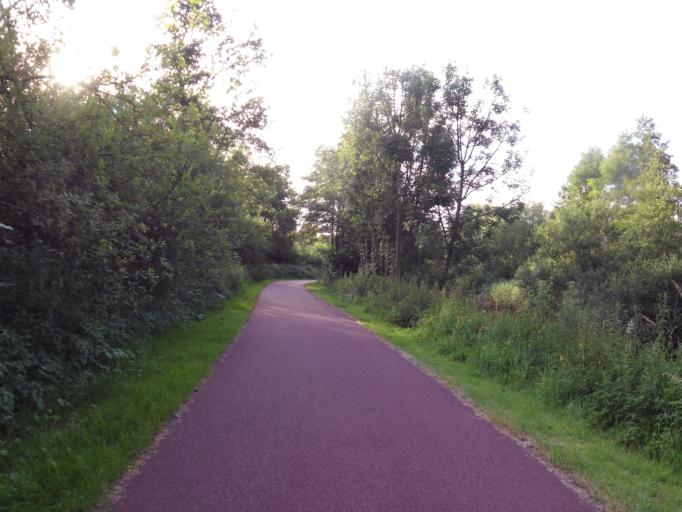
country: NL
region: North Brabant
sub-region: Gemeente Geldrop-Mierlo
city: Geldrop
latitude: 51.4314
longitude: 5.5507
